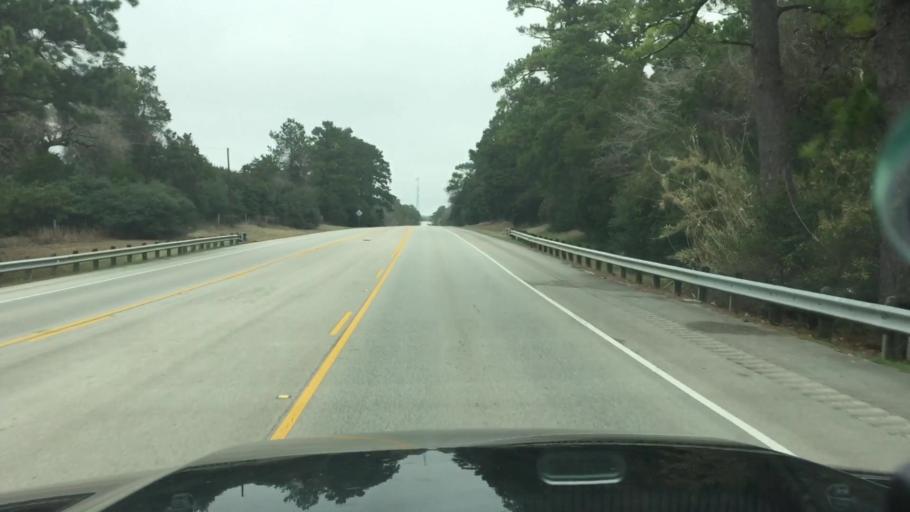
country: US
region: Texas
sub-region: Fayette County
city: La Grange
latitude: 30.0082
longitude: -96.8948
